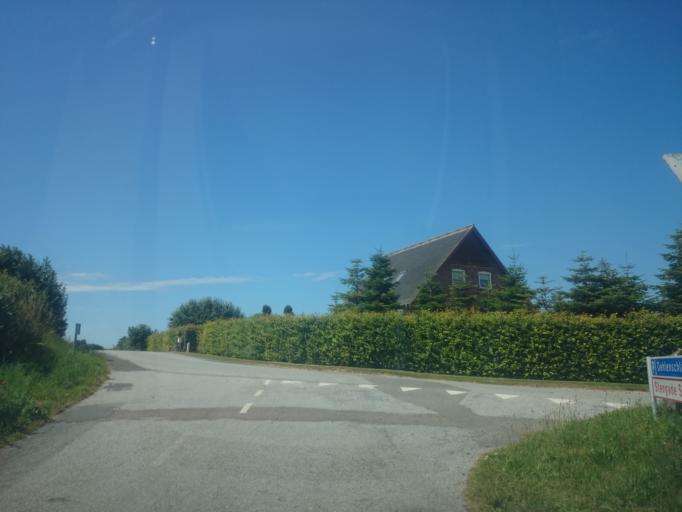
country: DK
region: South Denmark
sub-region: Langeland Kommune
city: Rudkobing
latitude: 54.9641
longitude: 10.8344
